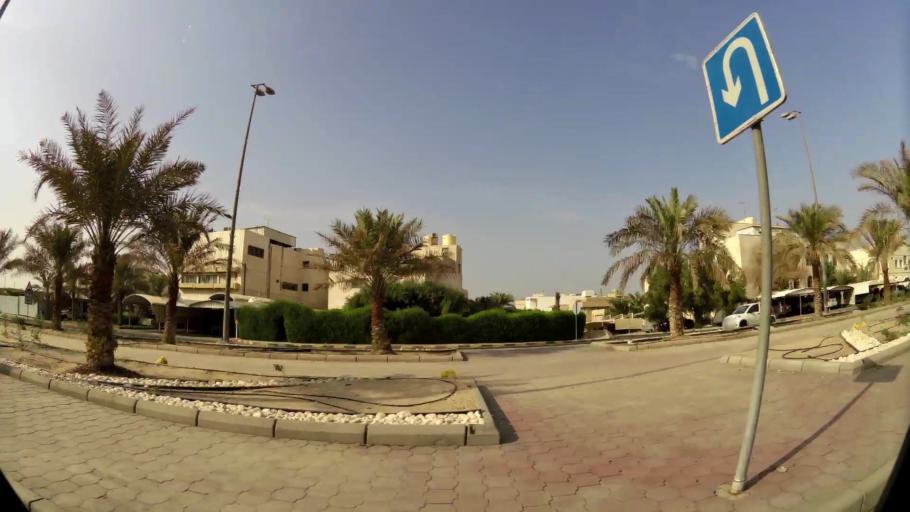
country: KW
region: Al Asimah
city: Ash Shamiyah
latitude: 29.3249
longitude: 47.9753
